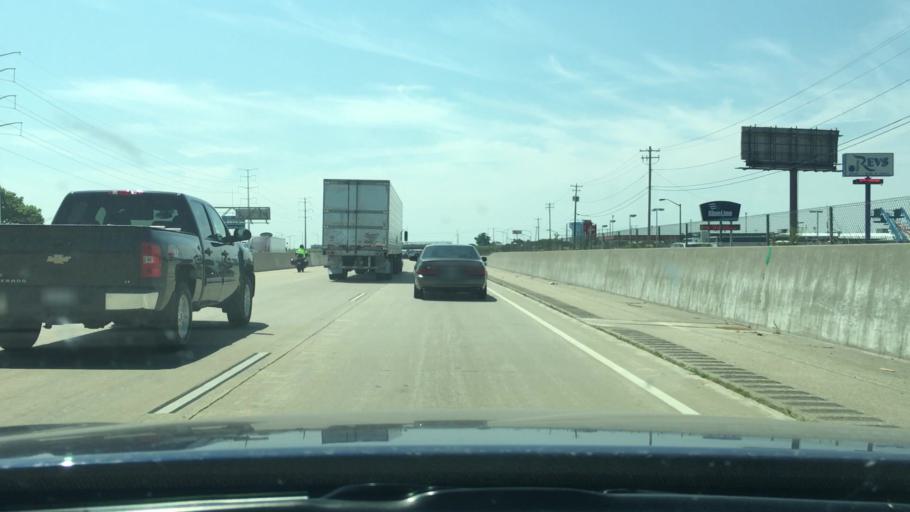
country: US
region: Wisconsin
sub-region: Winnebago County
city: Oshkosh
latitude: 44.0228
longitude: -88.5822
